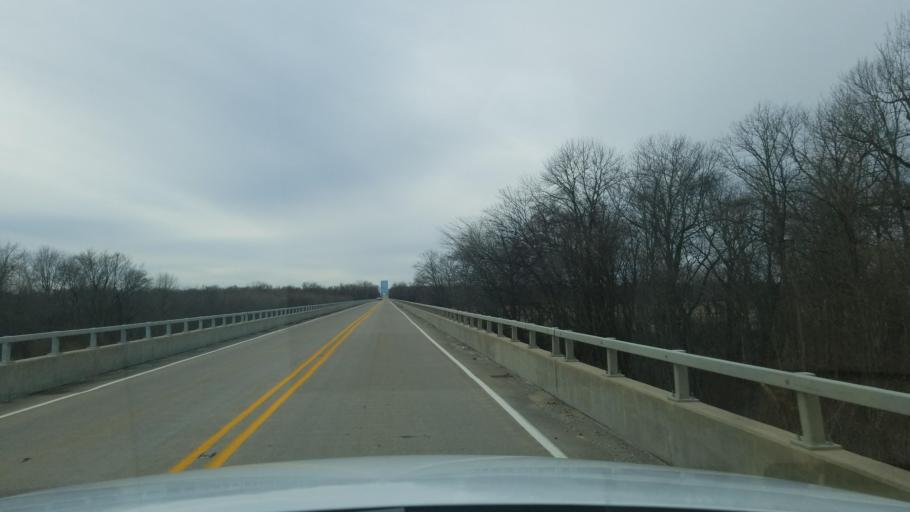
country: US
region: Indiana
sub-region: Posey County
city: Mount Vernon
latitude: 37.9443
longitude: -88.0231
